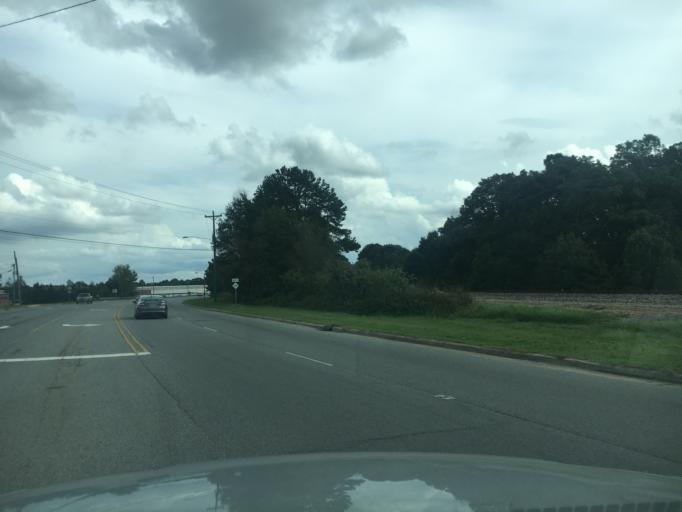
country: US
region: North Carolina
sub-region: Gaston County
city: Bessemer City
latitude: 35.2879
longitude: -81.2438
